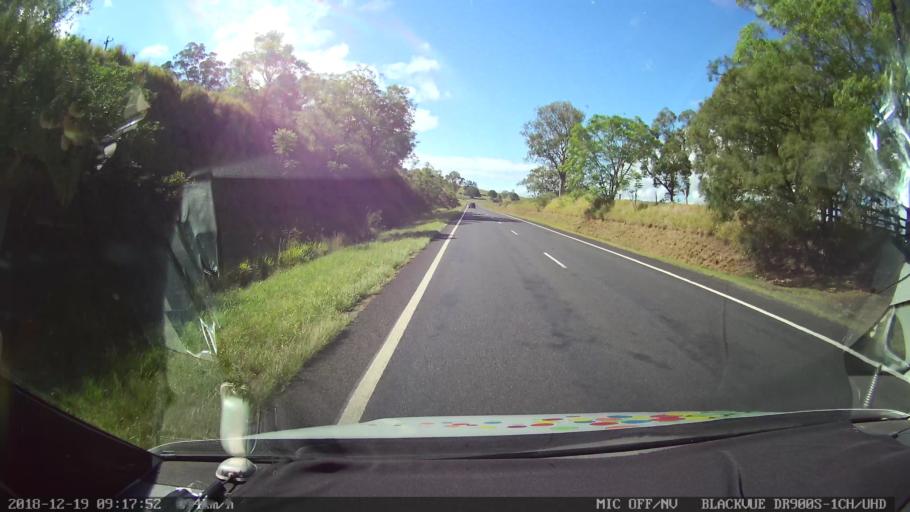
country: AU
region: New South Wales
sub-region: Kyogle
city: Kyogle
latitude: -28.5398
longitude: 152.9756
